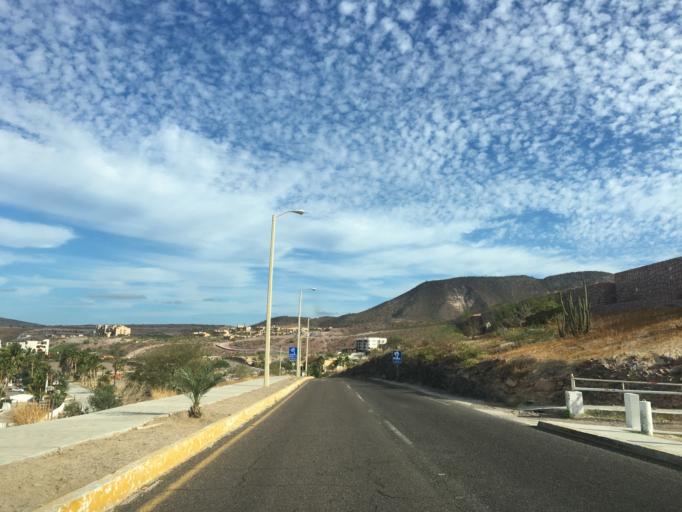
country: MX
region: Baja California Sur
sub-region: La Paz
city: La Paz
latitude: 24.2006
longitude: -110.2989
